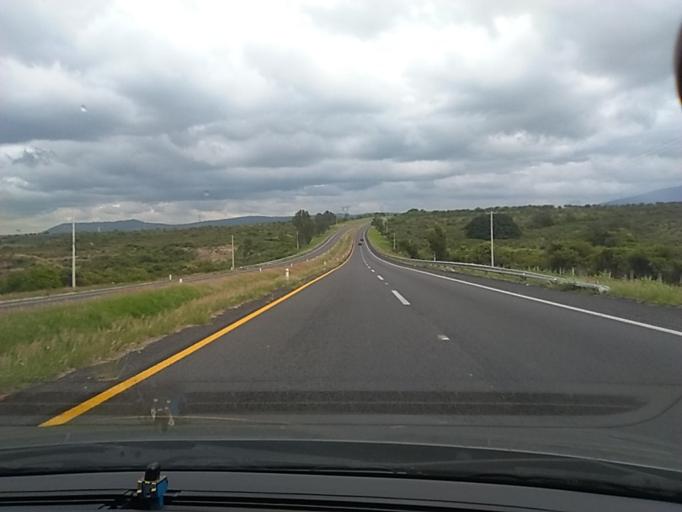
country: MX
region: Jalisco
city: Puente Grande
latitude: 20.6028
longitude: -103.1242
